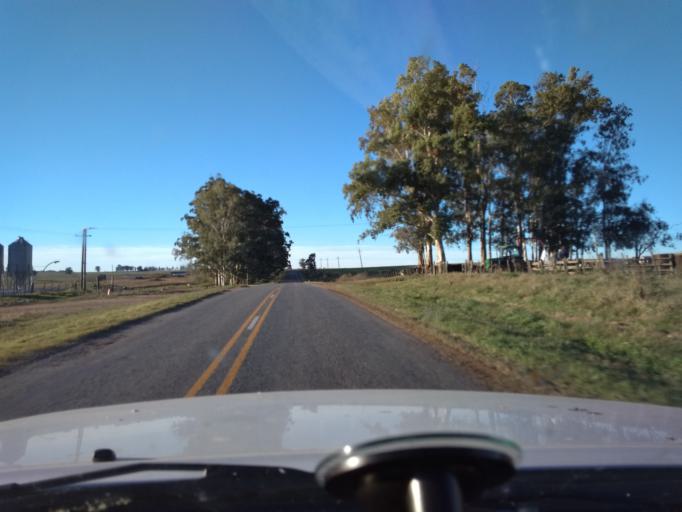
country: UY
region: Canelones
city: San Ramon
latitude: -34.0642
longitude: -55.9060
